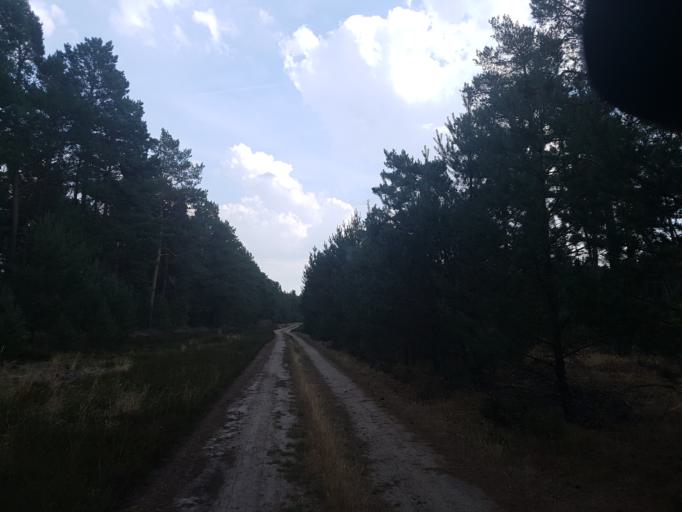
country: DE
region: Brandenburg
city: Treuenbrietzen
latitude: 52.0539
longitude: 12.8409
